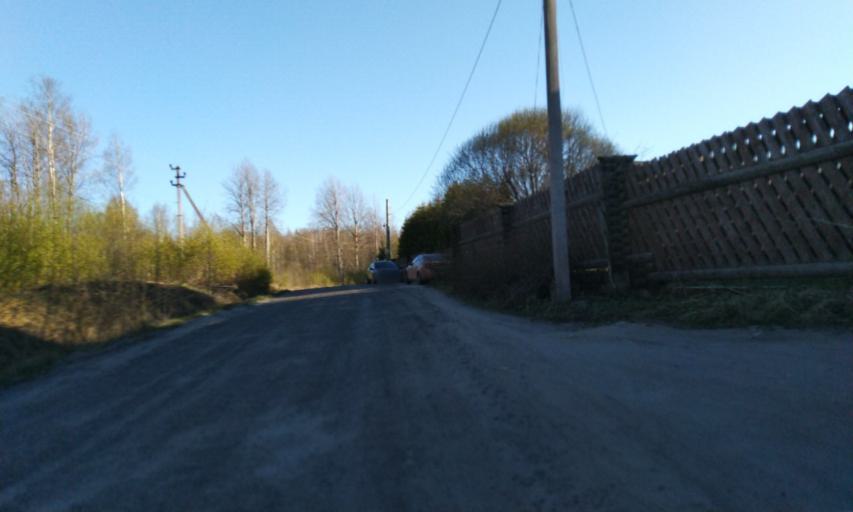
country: RU
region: Leningrad
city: Toksovo
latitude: 60.1494
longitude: 30.5810
